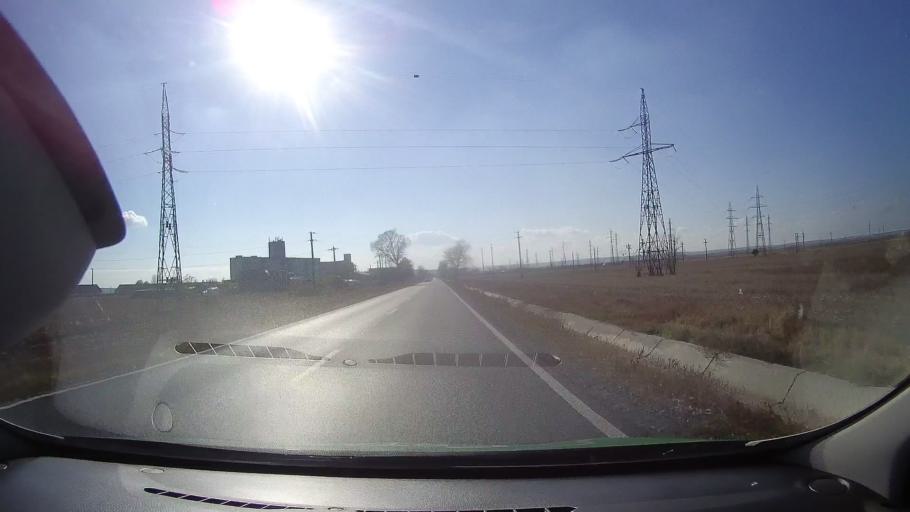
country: RO
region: Tulcea
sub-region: Comuna Baia
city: Baia
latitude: 44.7418
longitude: 28.6845
